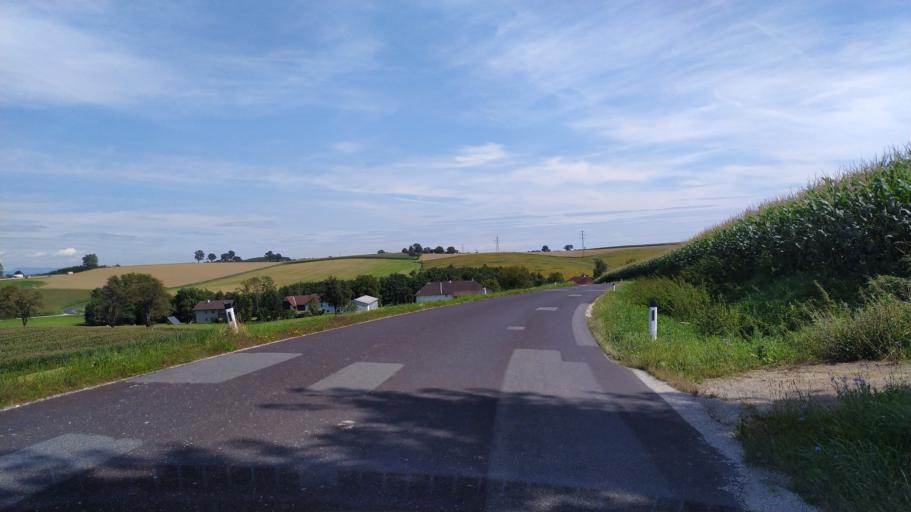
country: AT
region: Lower Austria
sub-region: Politischer Bezirk Amstetten
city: Wolfsbach
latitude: 48.1107
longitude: 14.6953
